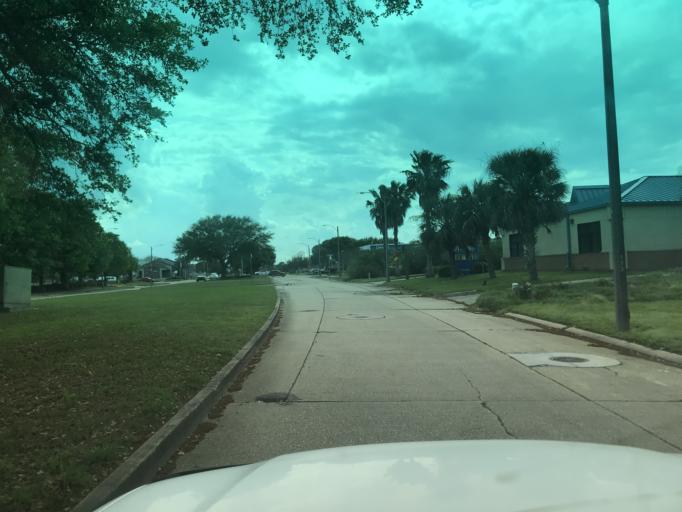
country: US
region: Louisiana
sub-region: Saint Bernard Parish
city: Chalmette
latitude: 30.0398
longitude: -89.9537
